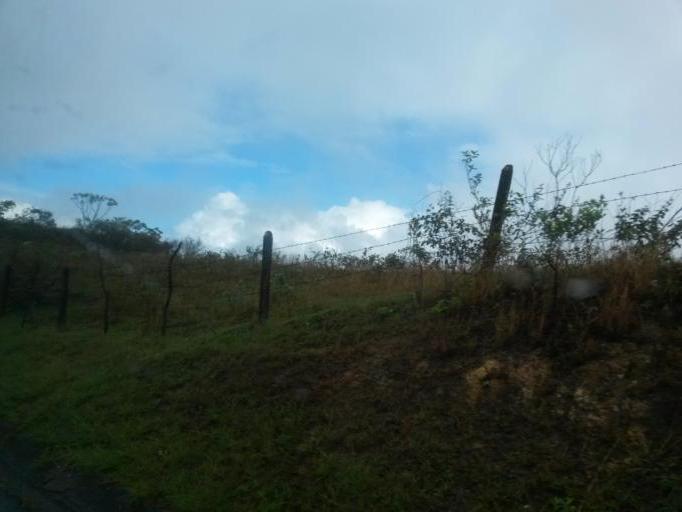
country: CO
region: Cauca
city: El Bordo
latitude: 2.1490
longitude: -76.9221
